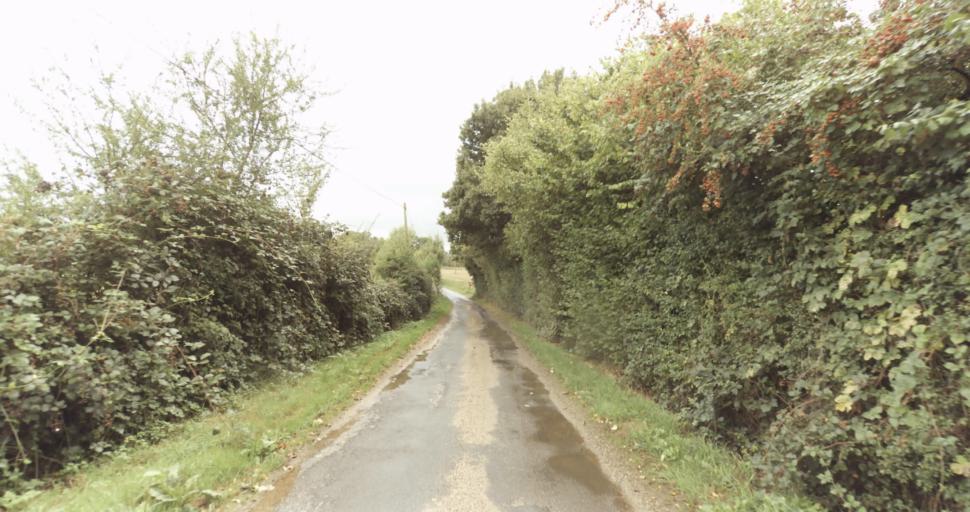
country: FR
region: Lower Normandy
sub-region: Departement de l'Orne
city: Sainte-Gauburge-Sainte-Colombe
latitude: 48.7121
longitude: 0.3970
